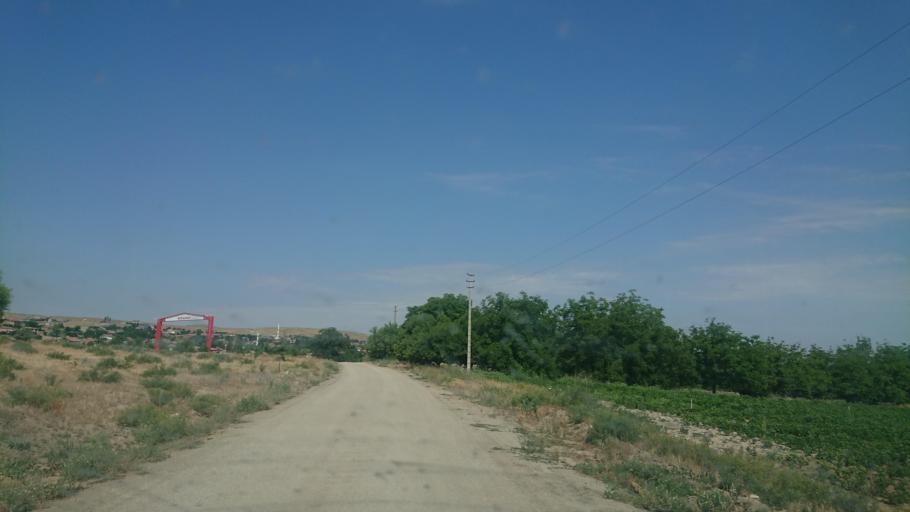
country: TR
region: Aksaray
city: Sariyahsi
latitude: 38.9574
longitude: 33.8952
